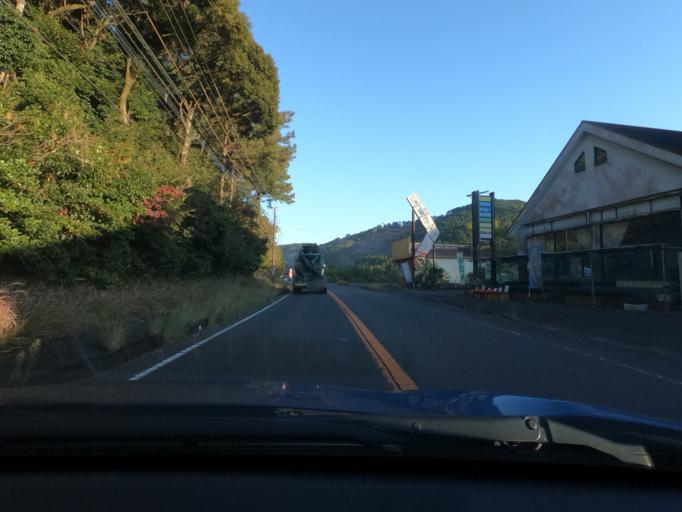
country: JP
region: Kagoshima
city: Satsumasendai
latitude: 31.8045
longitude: 130.3552
